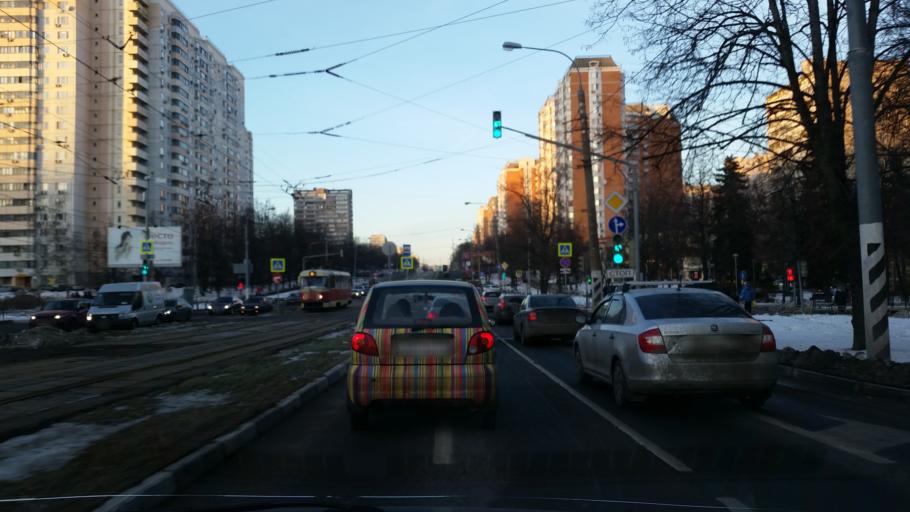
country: RU
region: Moscow
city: Nagornyy
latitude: 55.6445
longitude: 37.6057
